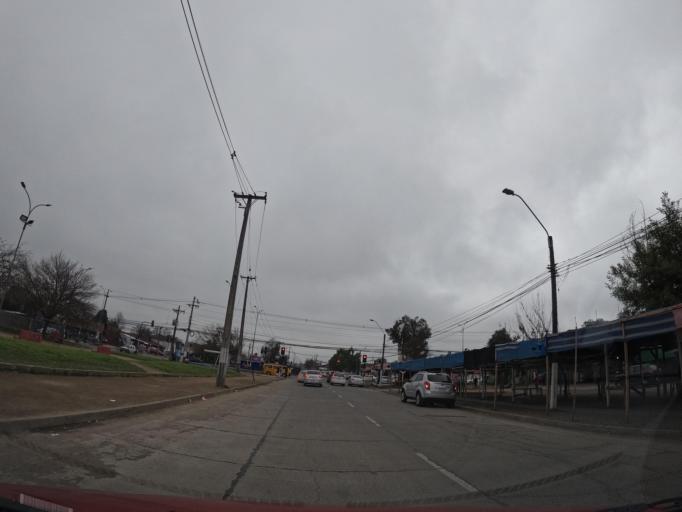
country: CL
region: Maule
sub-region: Provincia de Talca
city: Talca
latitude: -35.4413
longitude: -71.6334
